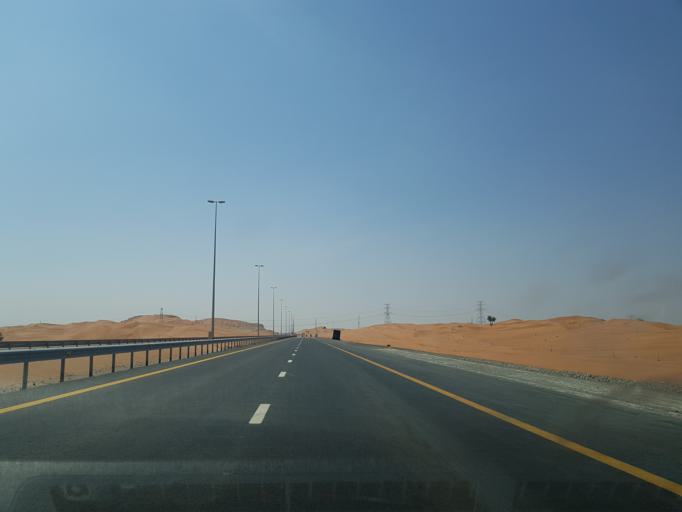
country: AE
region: Ash Shariqah
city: Adh Dhayd
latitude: 25.2451
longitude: 55.8560
